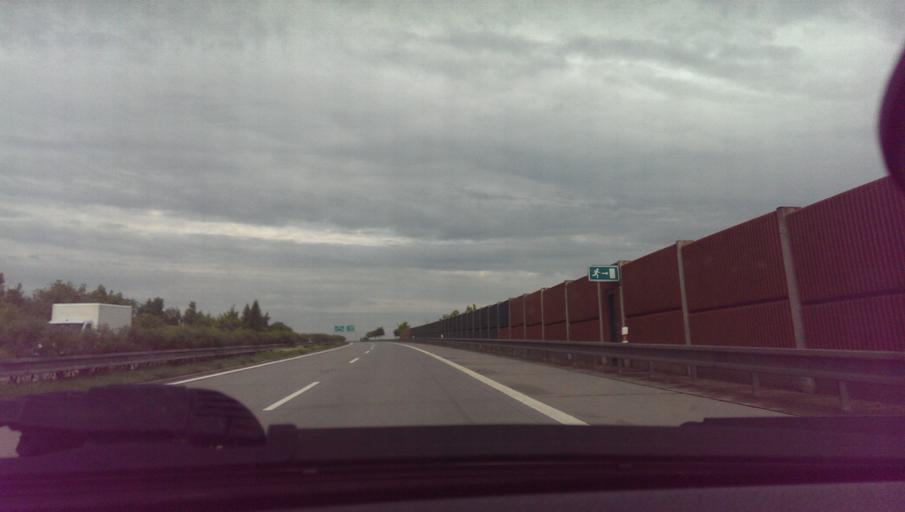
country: CZ
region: South Moravian
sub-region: Okres Vyskov
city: Vyskov
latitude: 49.2732
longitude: 17.0331
